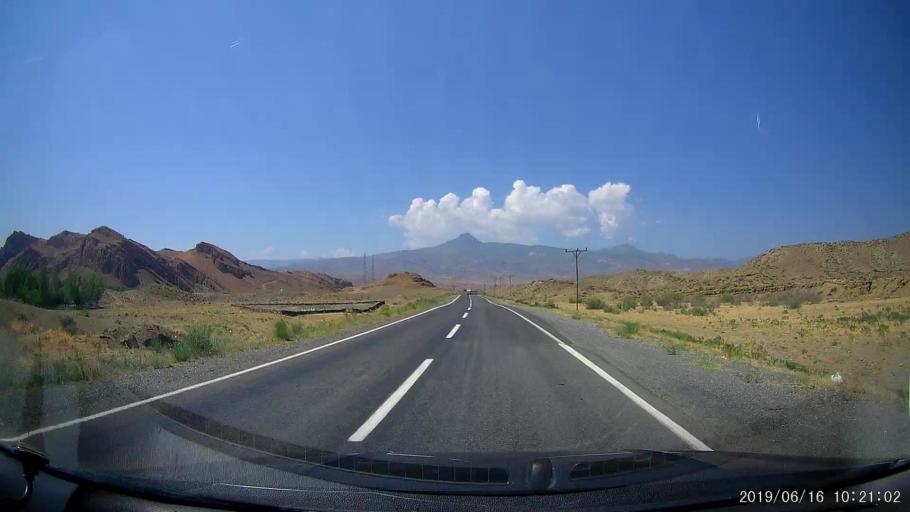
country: TR
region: Igdir
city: Tuzluca
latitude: 40.1418
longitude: 43.6412
